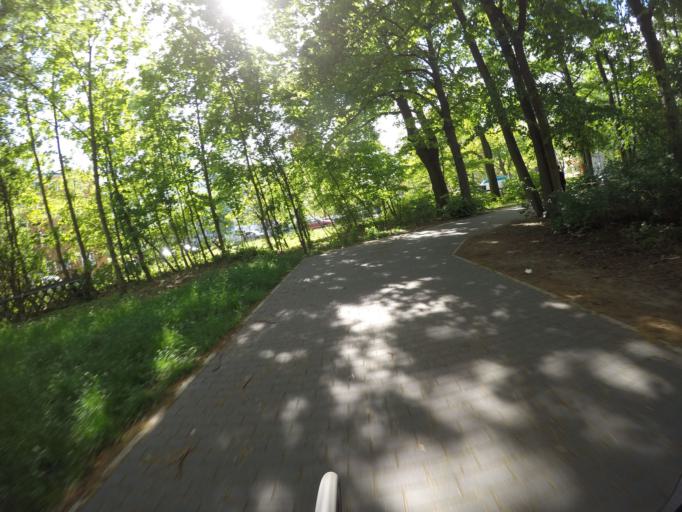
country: DE
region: Berlin
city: Lichtenrade
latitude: 52.4232
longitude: 13.4156
